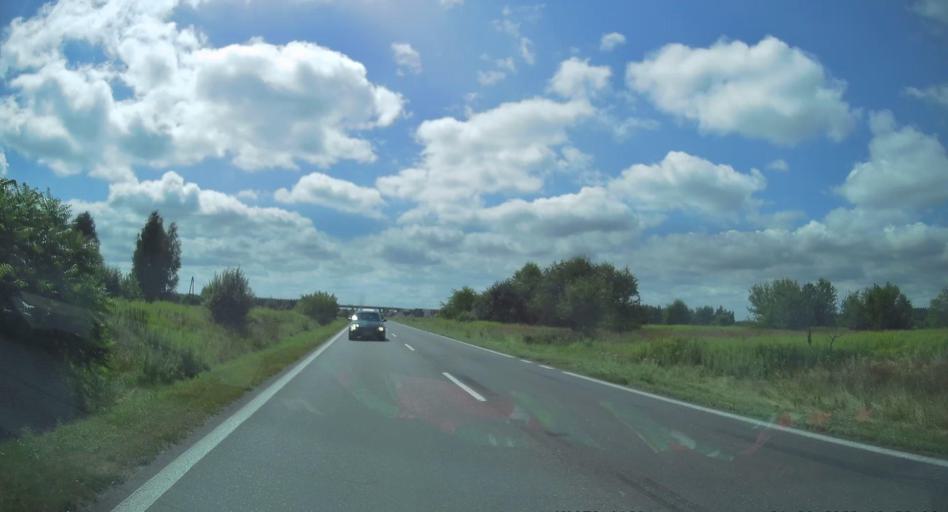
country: PL
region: Subcarpathian Voivodeship
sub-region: Powiat mielecki
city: Padew Narodowa
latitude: 50.3883
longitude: 21.4613
